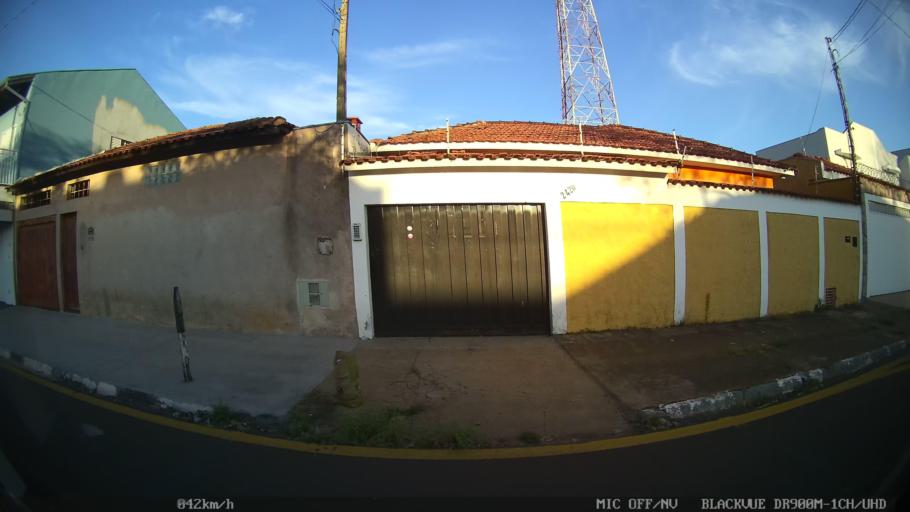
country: BR
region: Sao Paulo
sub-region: Franca
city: Franca
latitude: -20.5129
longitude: -47.3868
